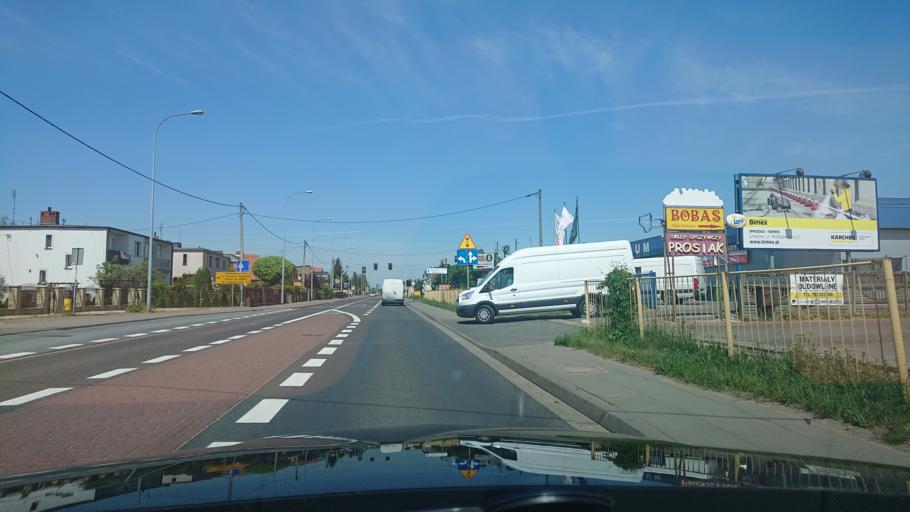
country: PL
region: Greater Poland Voivodeship
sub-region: Powiat gnieznienski
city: Gniezno
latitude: 52.5129
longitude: 17.6151
